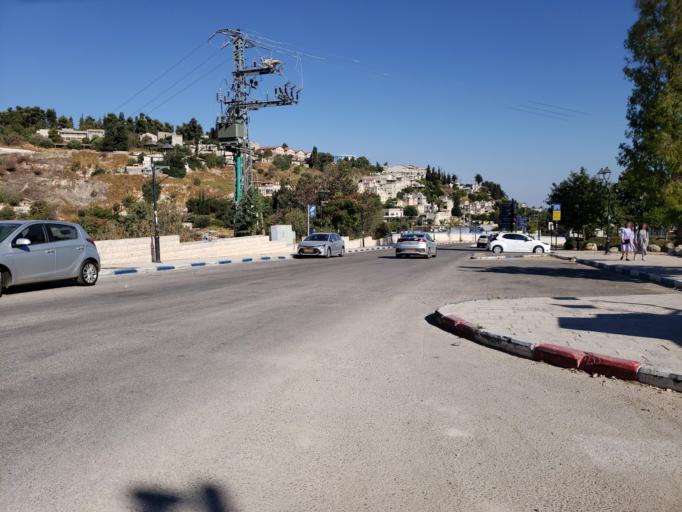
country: IL
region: Northern District
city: Safed
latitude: 32.9707
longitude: 35.4962
